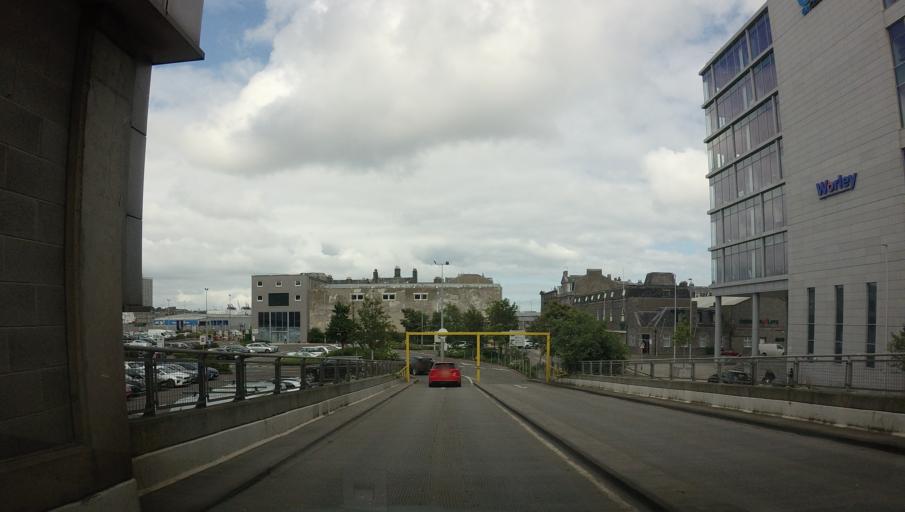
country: GB
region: Scotland
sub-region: Aberdeen City
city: Aberdeen
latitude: 57.1419
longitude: -2.0948
